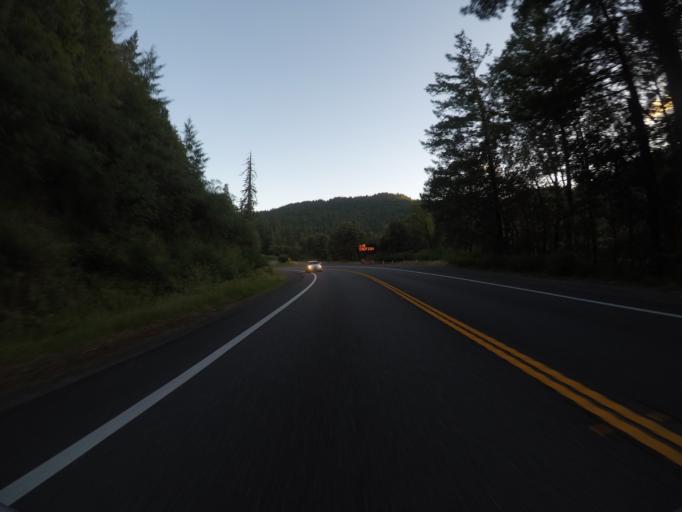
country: US
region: California
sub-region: Humboldt County
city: Redway
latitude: 39.9081
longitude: -123.7590
